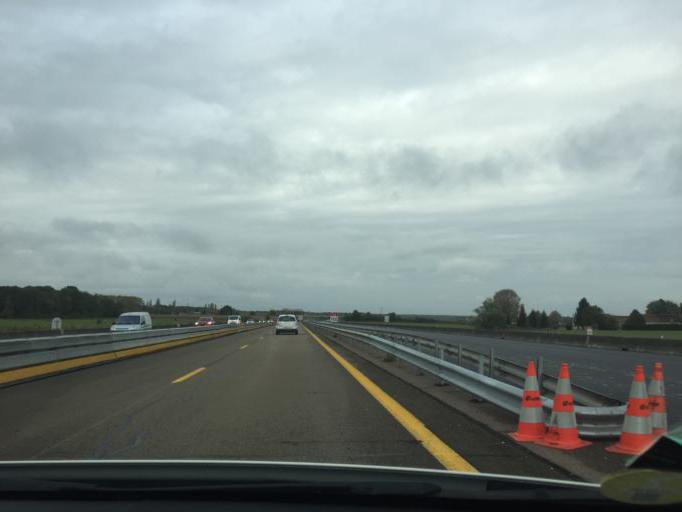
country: FR
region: Bourgogne
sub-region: Departement de l'Yonne
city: Saint-Julien-du-Sault
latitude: 47.9795
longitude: 3.1914
